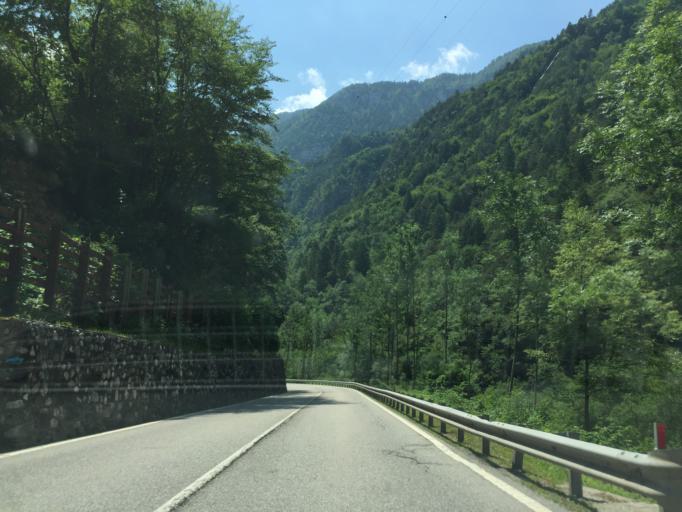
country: IT
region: Trentino-Alto Adige
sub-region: Provincia di Trento
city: Imer
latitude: 46.1373
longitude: 11.7699
